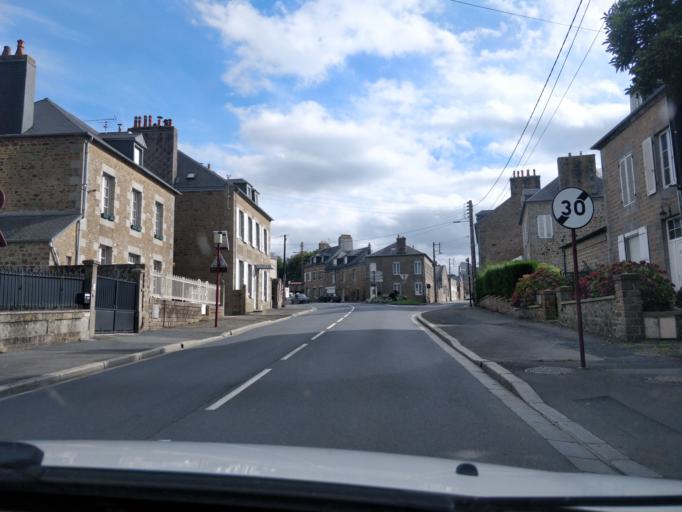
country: FR
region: Lower Normandy
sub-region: Departement du Calvados
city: Vire
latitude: 48.8410
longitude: -0.8961
